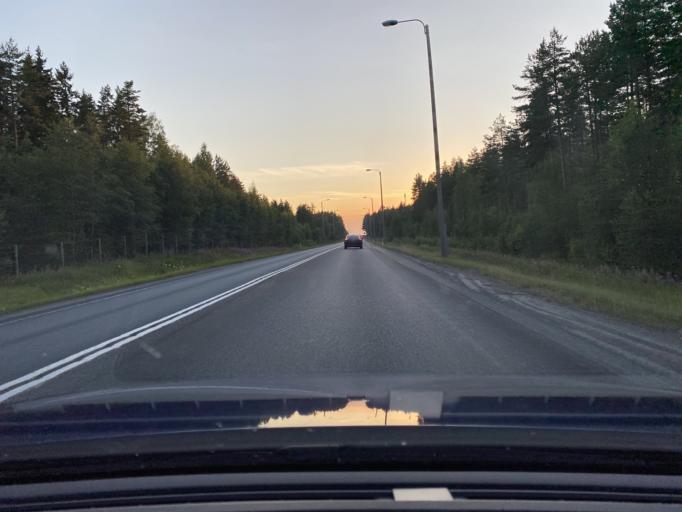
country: FI
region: Pirkanmaa
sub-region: Luoteis-Pirkanmaa
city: Ikaalinen
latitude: 61.7406
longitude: 23.1135
